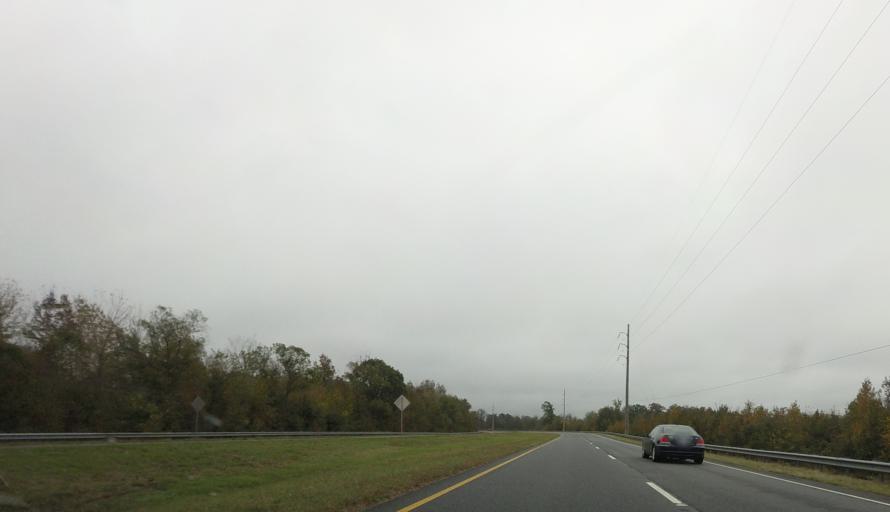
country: US
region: Georgia
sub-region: Taylor County
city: Reynolds
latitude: 32.5416
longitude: -84.0277
